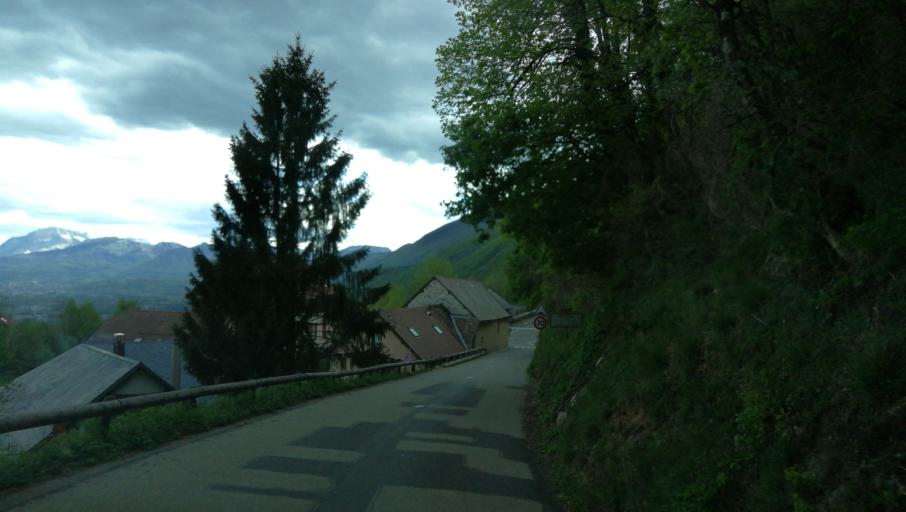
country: FR
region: Rhone-Alpes
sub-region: Departement de la Savoie
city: Le Bourget-du-Lac
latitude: 45.6926
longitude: 5.8533
